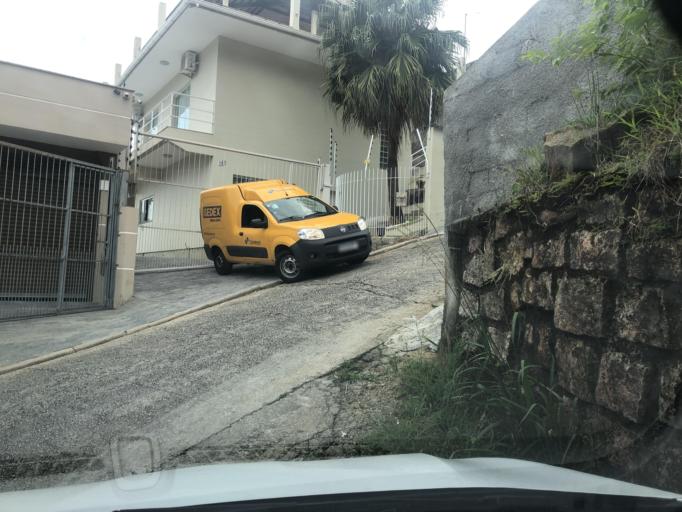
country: BR
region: Santa Catarina
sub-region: Florianopolis
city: Saco dos Limoes
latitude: -27.6011
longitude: -48.5372
